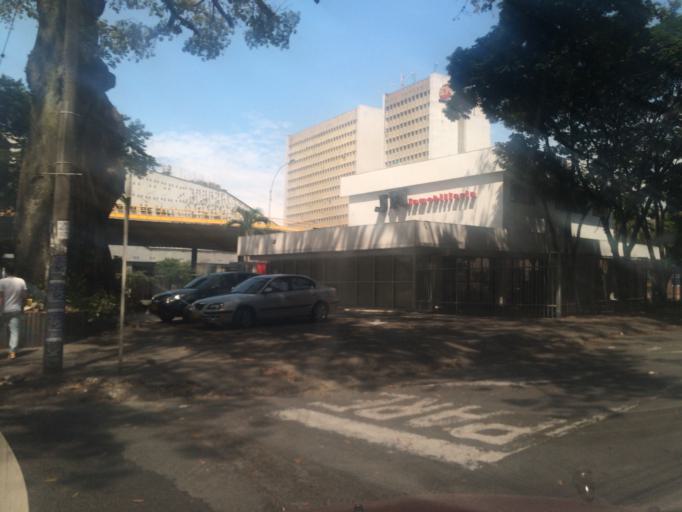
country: CO
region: Valle del Cauca
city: Cali
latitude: 3.4550
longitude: -76.5361
